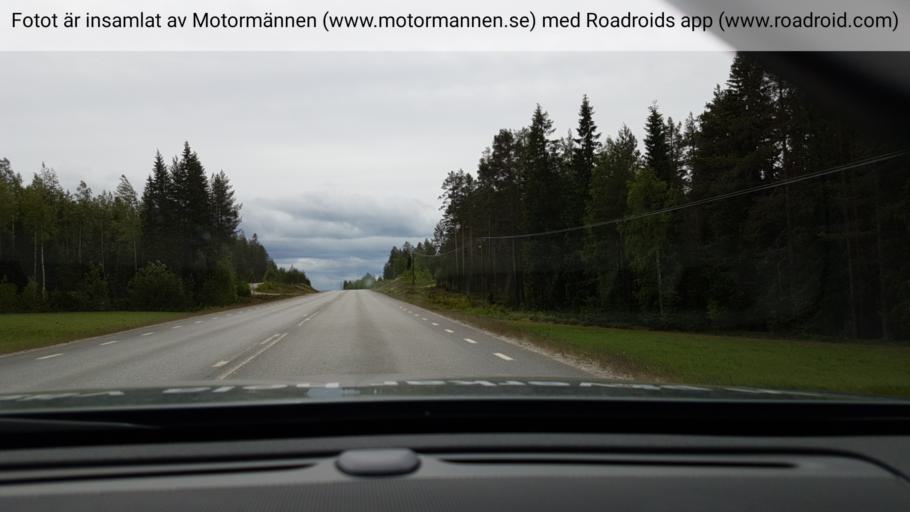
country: SE
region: Vaesterbotten
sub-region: Vannas Kommun
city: Vaennaes
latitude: 64.0356
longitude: 19.6923
